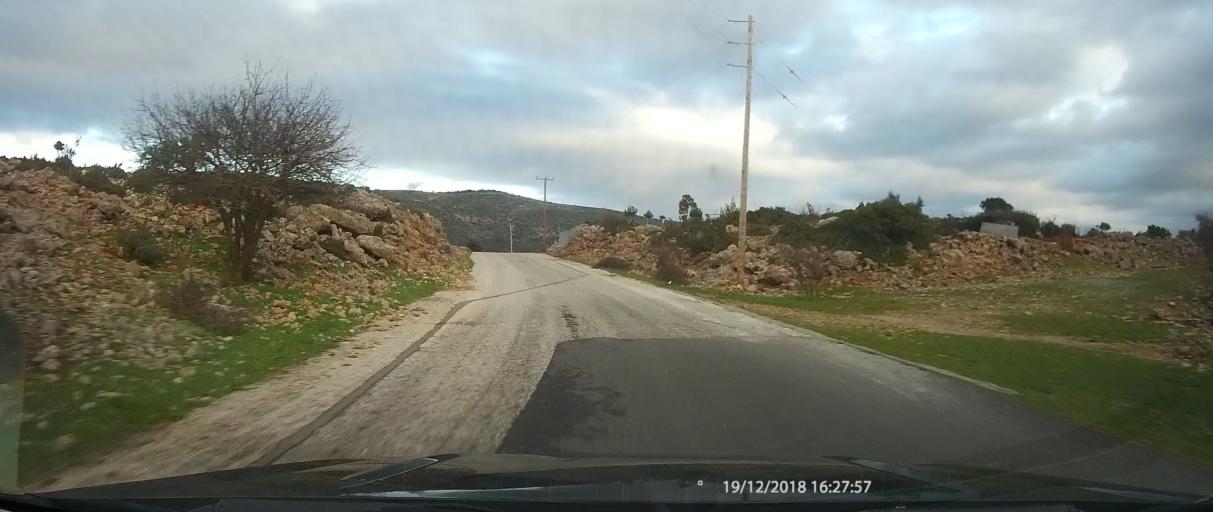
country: GR
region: Peloponnese
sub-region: Nomos Lakonias
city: Kato Glikovrisi
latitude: 36.9611
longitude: 22.8613
